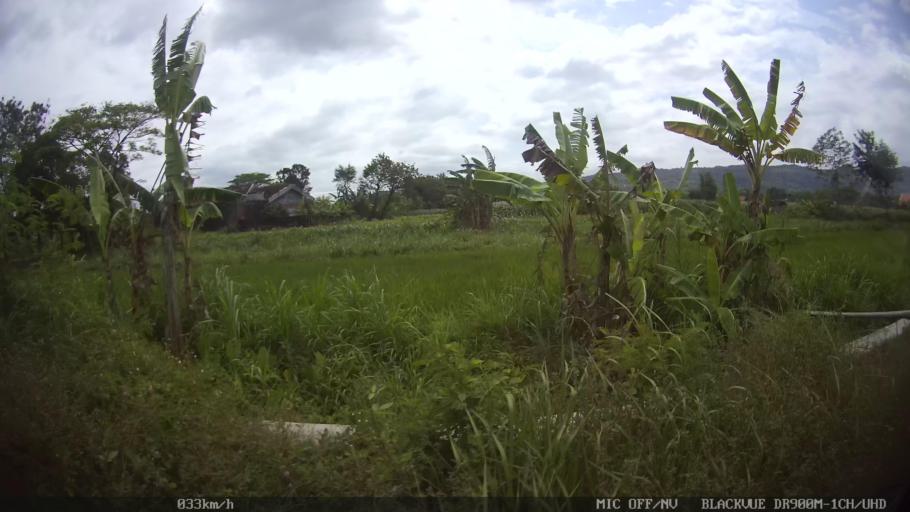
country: ID
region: Central Java
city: Candi Prambanan
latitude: -7.8123
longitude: 110.4912
